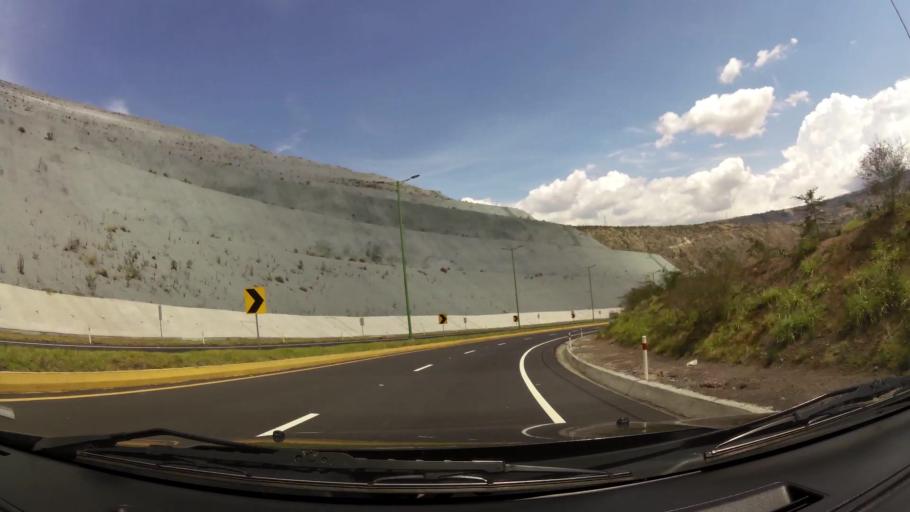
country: EC
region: Pichincha
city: Quito
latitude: -0.1046
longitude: -78.3760
